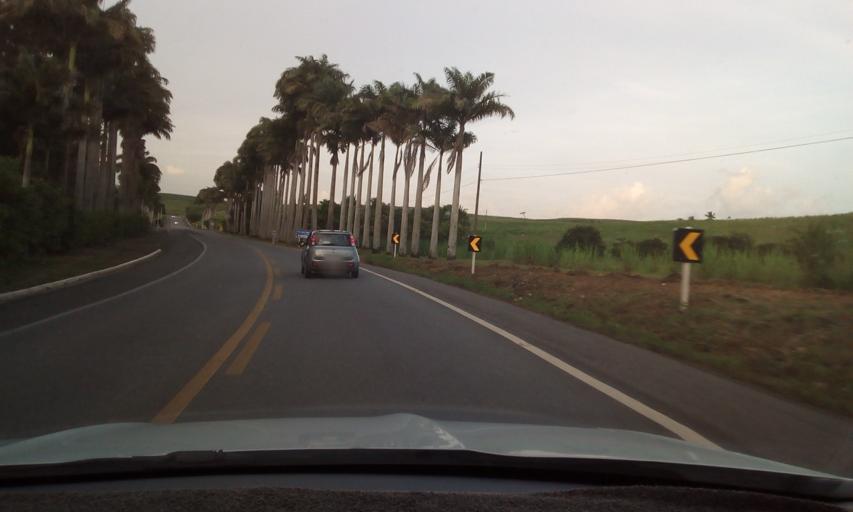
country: BR
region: Pernambuco
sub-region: Vicencia
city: Vicencia
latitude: -7.6291
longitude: -35.2475
